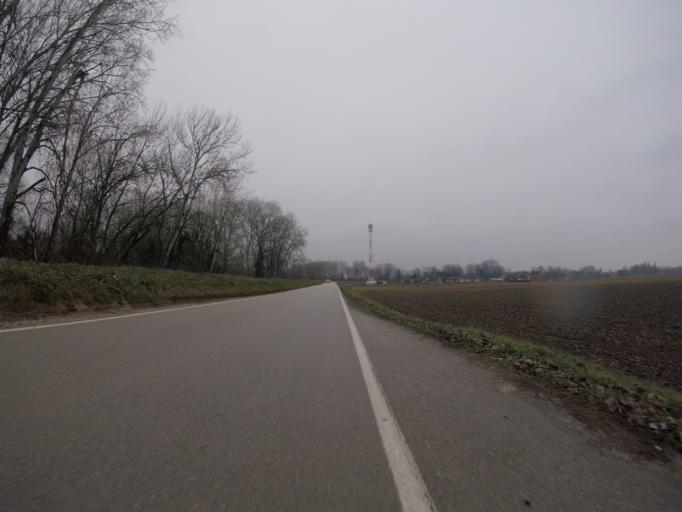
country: HR
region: Zagrebacka
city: Kuce
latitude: 45.6889
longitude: 16.2395
